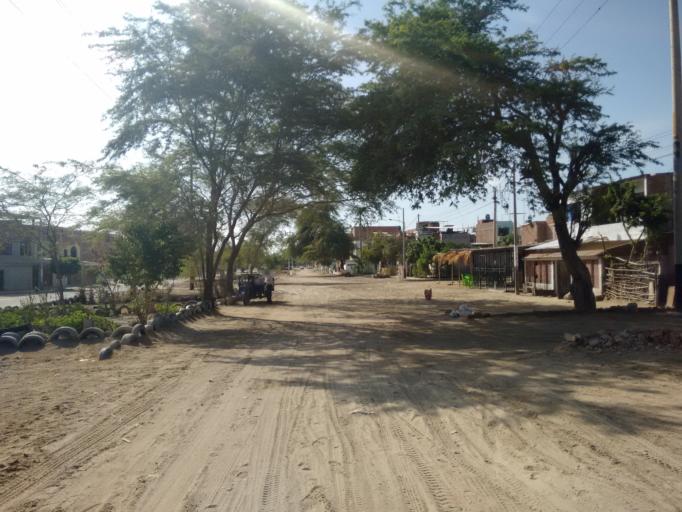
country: PE
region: Piura
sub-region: Provincia de Piura
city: Piura
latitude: -5.1737
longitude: -80.6439
